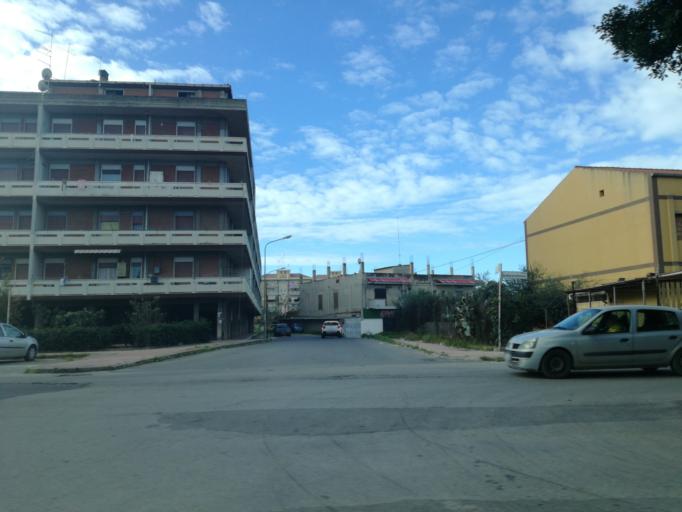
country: IT
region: Sicily
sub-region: Provincia di Caltanissetta
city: Gela
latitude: 37.0775
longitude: 14.2189
